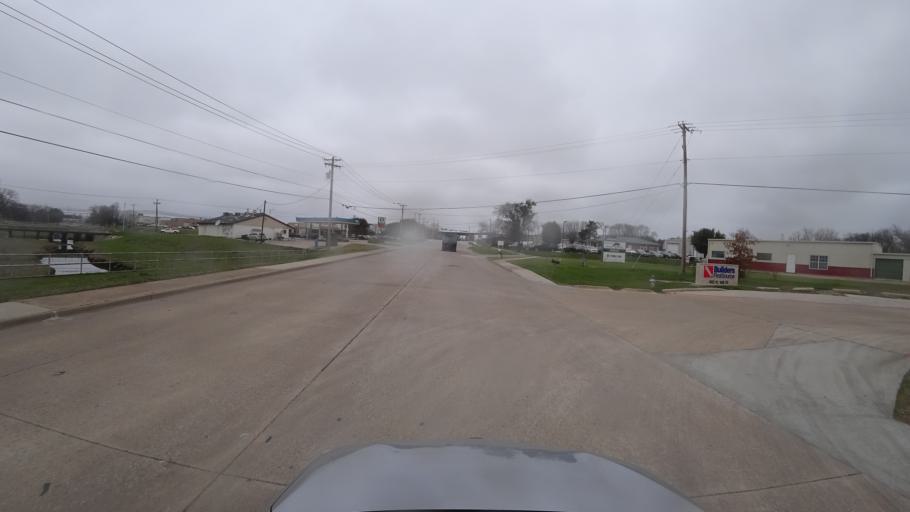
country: US
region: Texas
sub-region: Denton County
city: Lewisville
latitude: 33.0564
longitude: -96.9999
